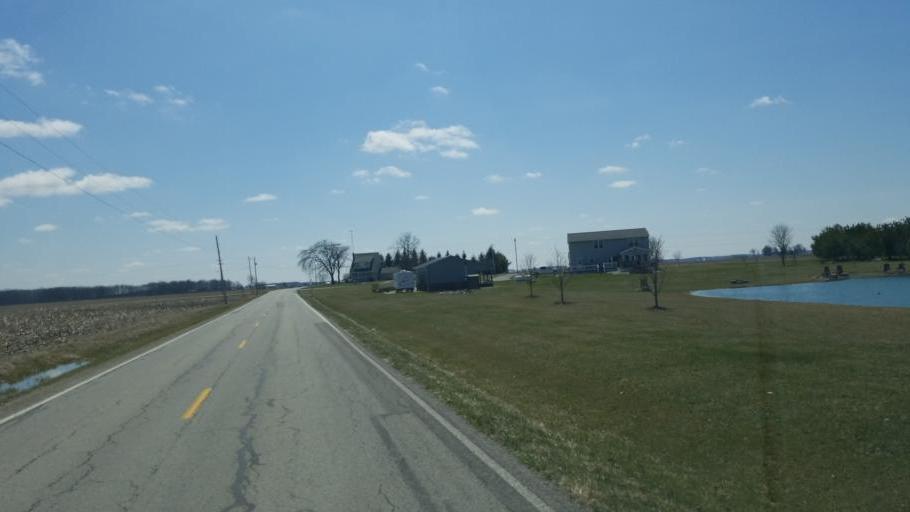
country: US
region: Ohio
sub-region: Wyandot County
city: Upper Sandusky
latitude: 40.6896
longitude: -83.2398
